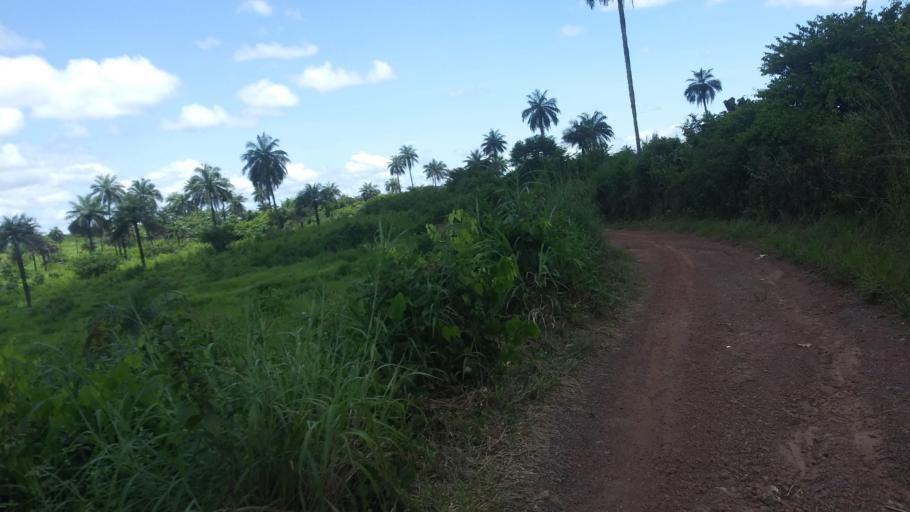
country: SL
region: Northern Province
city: Makeni
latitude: 8.8982
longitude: -11.9961
